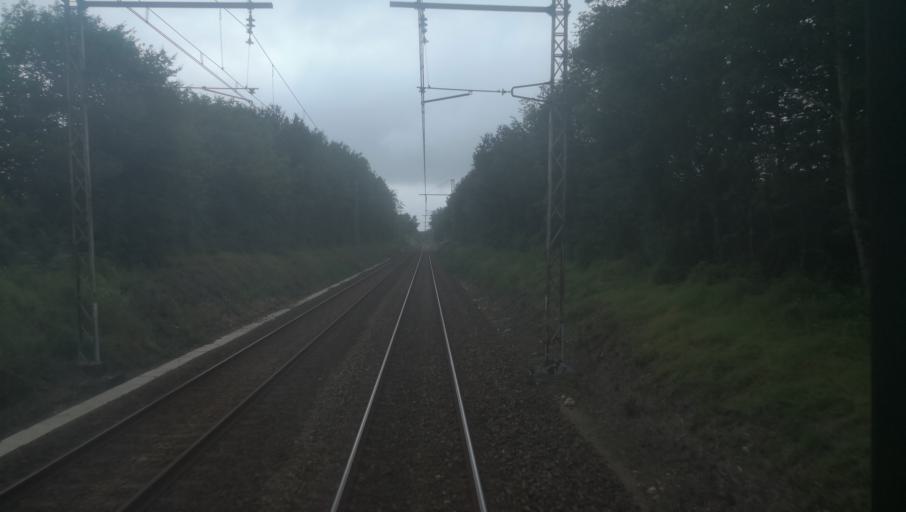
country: FR
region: Centre
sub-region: Departement de l'Indre
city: Luant
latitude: 46.7307
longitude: 1.5872
